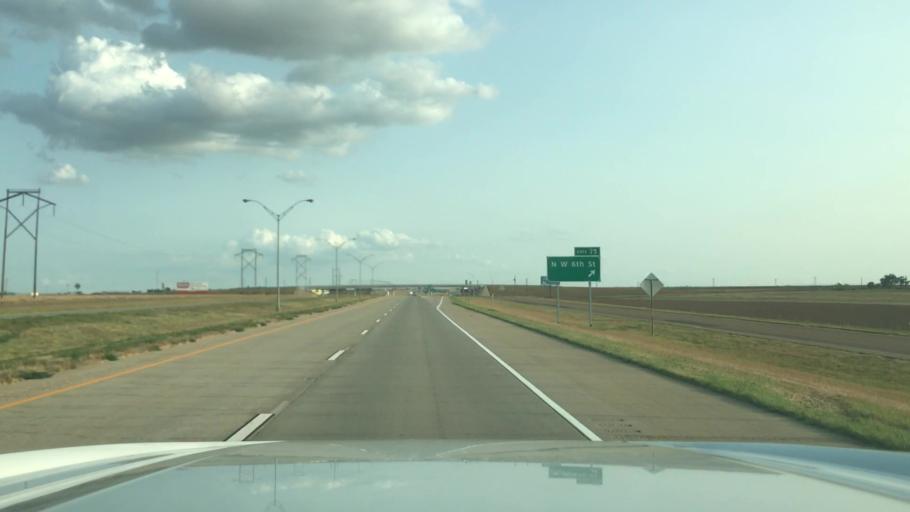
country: US
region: Texas
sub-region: Swisher County
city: Tulia
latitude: 34.5496
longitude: -101.7950
